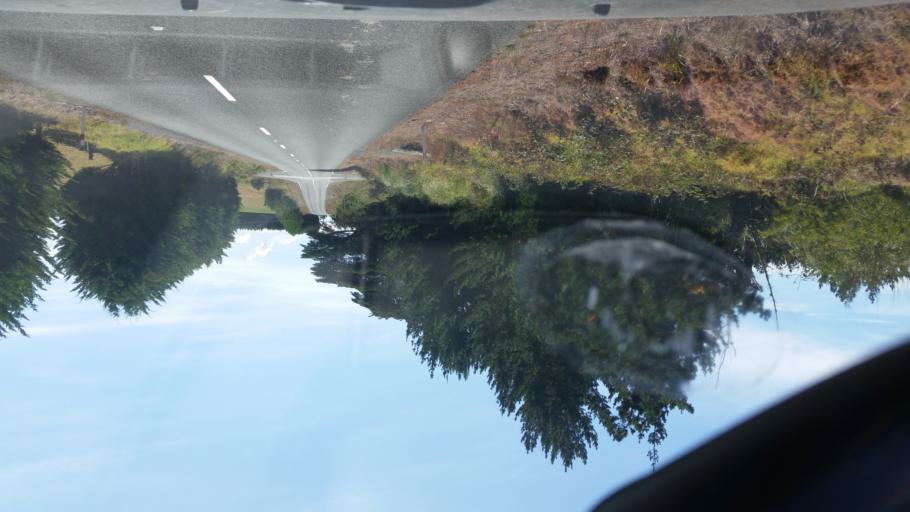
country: NZ
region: Auckland
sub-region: Auckland
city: Wellsford
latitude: -36.1997
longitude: 174.1681
